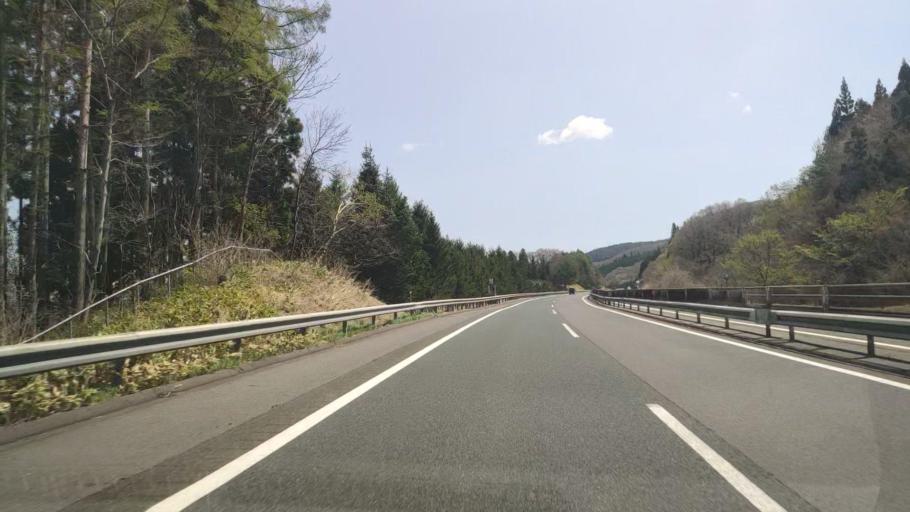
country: JP
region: Iwate
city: Ichinohe
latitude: 40.1185
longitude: 141.0829
